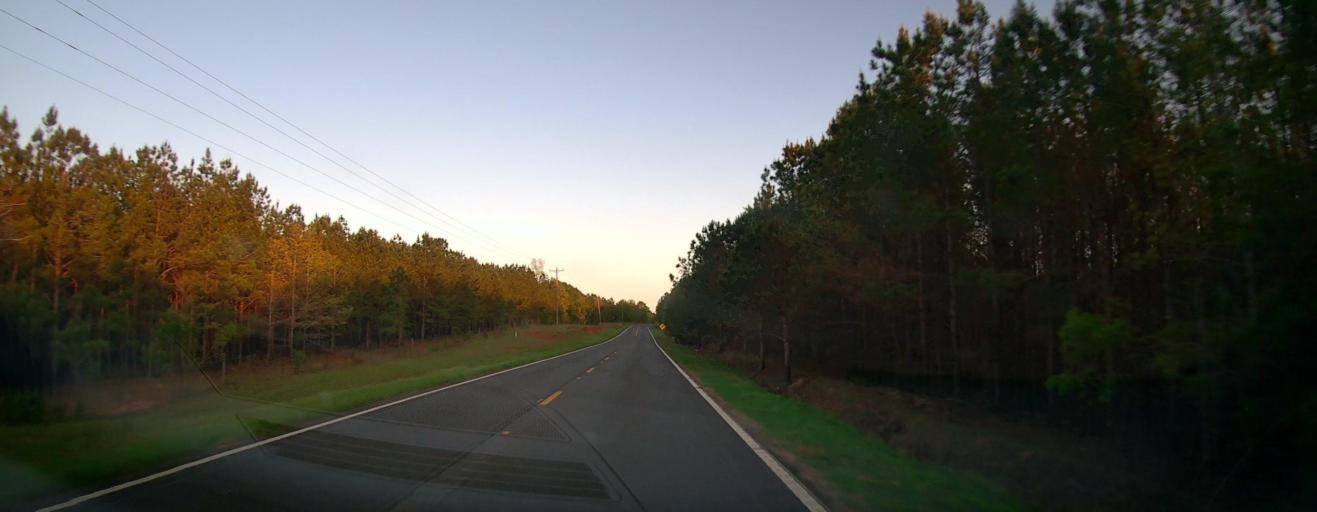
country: US
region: Georgia
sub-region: Marion County
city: Buena Vista
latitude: 32.3922
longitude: -84.5697
